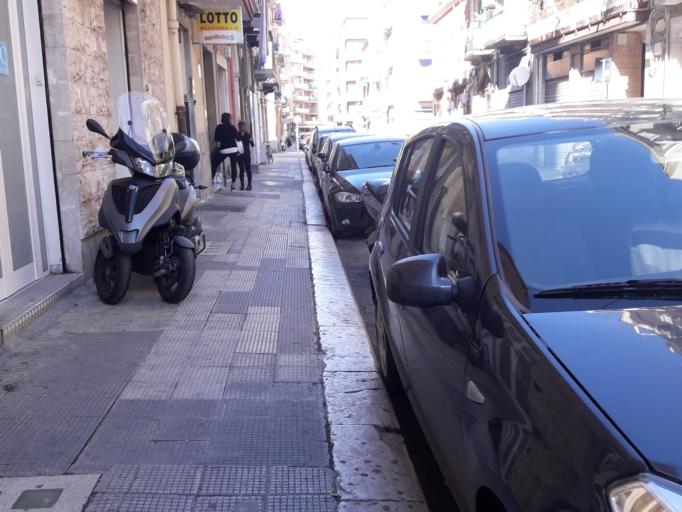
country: IT
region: Apulia
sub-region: Provincia di Bari
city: Bari
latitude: 41.1230
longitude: 16.8540
